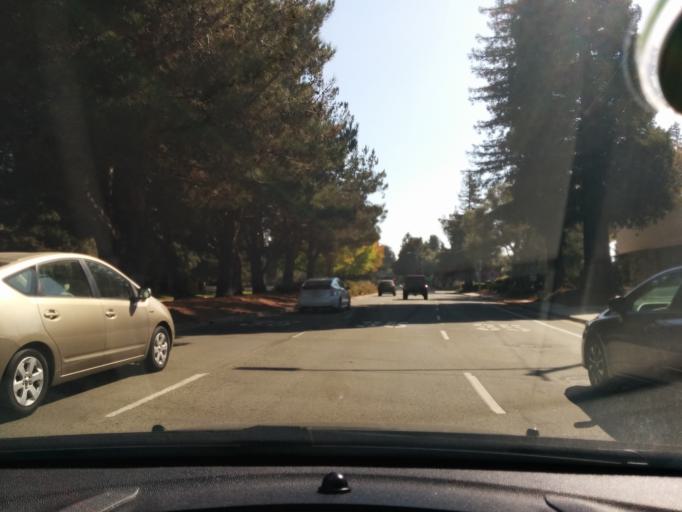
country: US
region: California
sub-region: Santa Clara County
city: Sunnyvale
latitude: 37.3806
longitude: -122.0121
